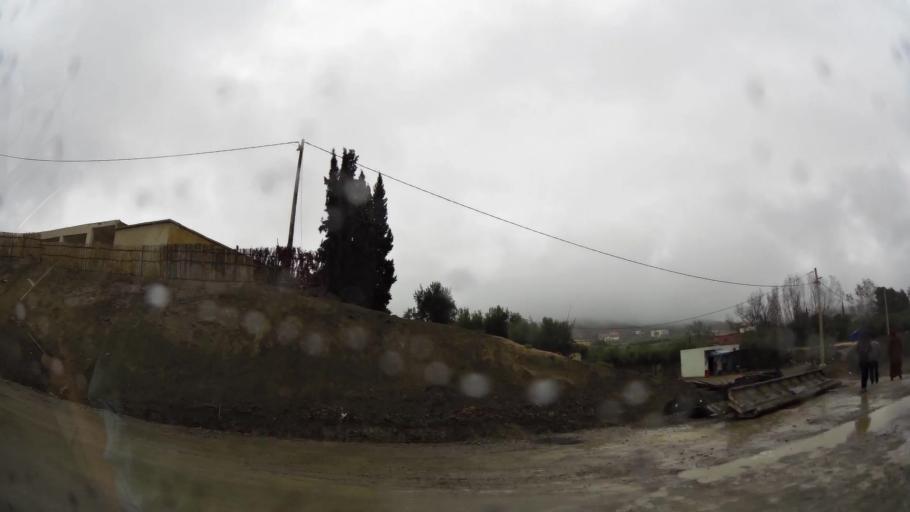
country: MA
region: Taza-Al Hoceima-Taounate
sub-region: Taza
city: Aknoul
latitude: 34.8090
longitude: -3.7358
